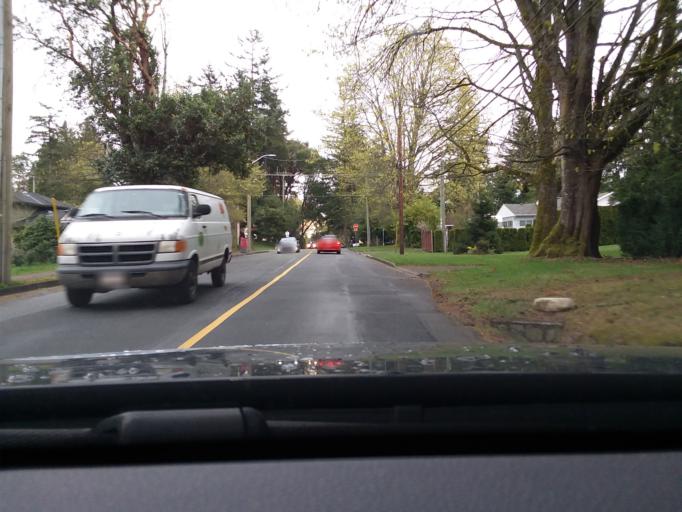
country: CA
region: British Columbia
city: Victoria
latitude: 48.5142
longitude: -123.3753
